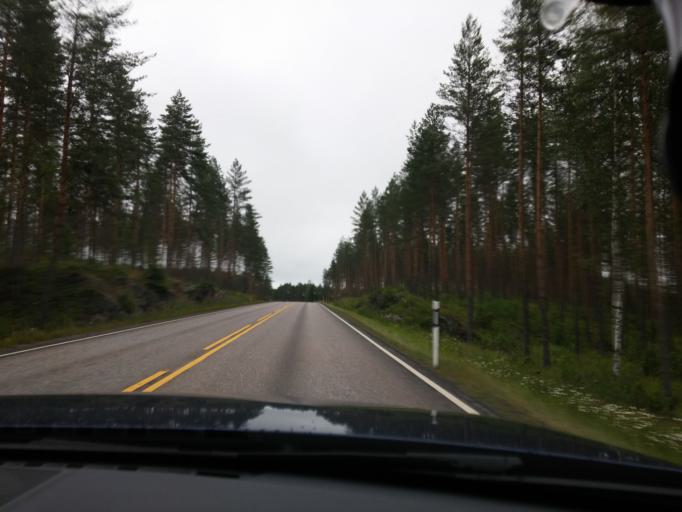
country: FI
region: Pirkanmaa
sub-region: Ylae-Pirkanmaa
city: Vilppula
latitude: 61.9204
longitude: 24.5371
